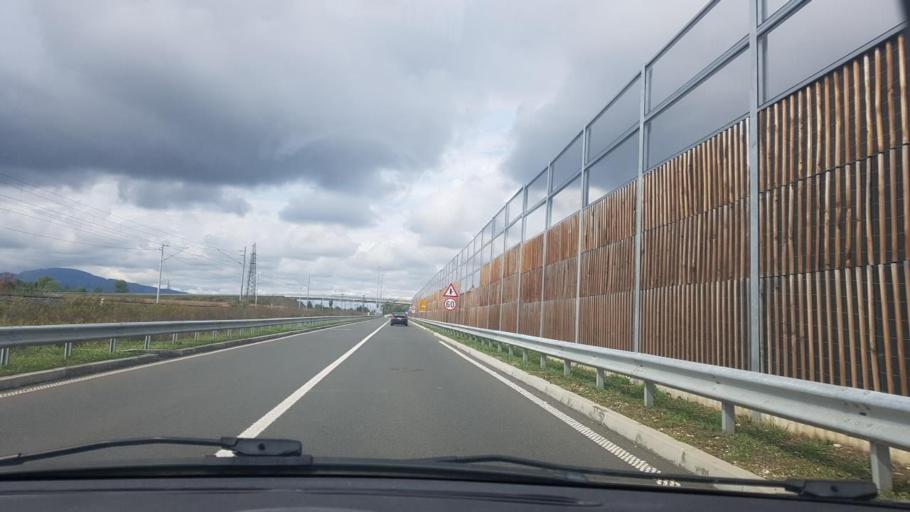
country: HR
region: Zagrebacka
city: Brdovec
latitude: 45.8563
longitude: 15.7909
